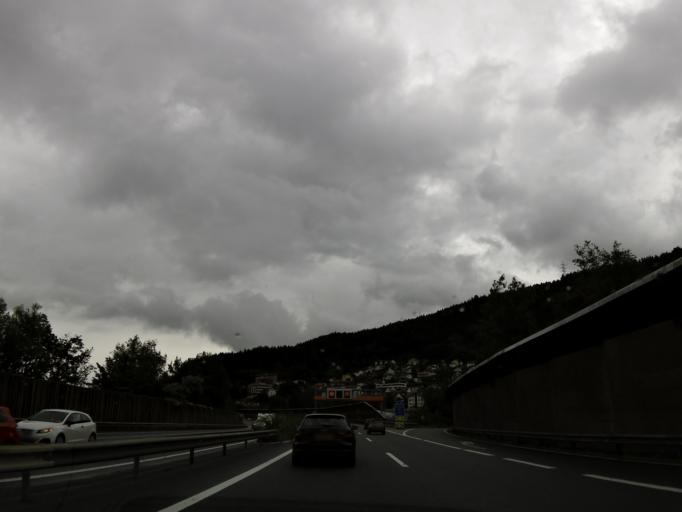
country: AT
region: Tyrol
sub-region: Politischer Bezirk Innsbruck Land
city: Natters
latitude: 47.2527
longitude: 11.3661
